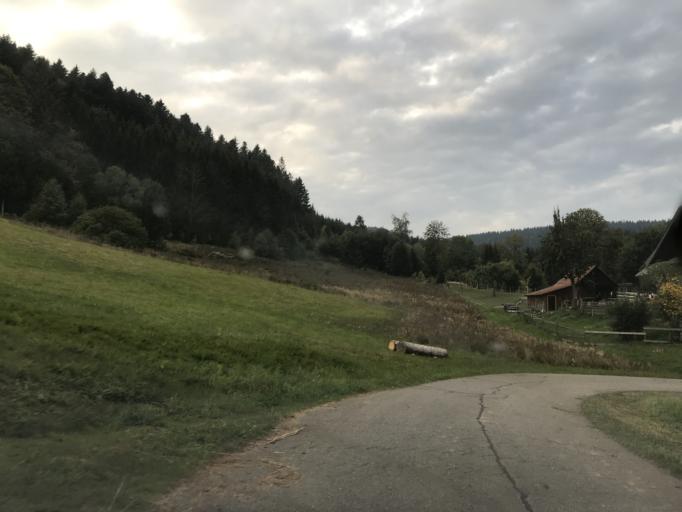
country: DE
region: Baden-Wuerttemberg
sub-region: Freiburg Region
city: Todtmoos
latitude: 47.7211
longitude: 7.9837
